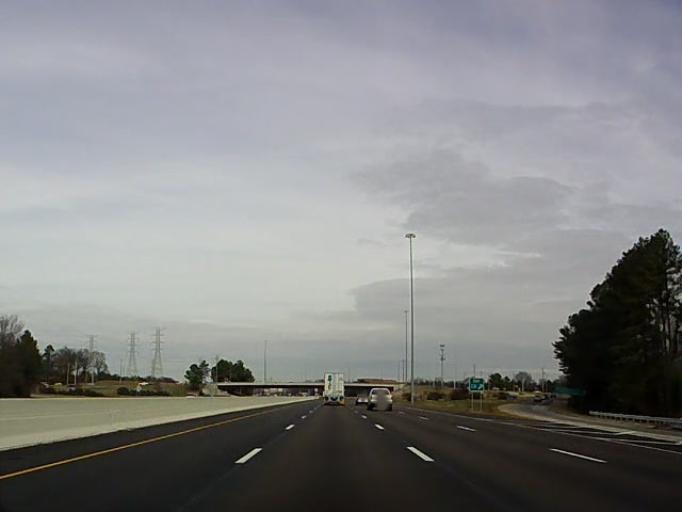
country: US
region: Tennessee
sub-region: Shelby County
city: Germantown
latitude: 35.1293
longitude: -89.8677
